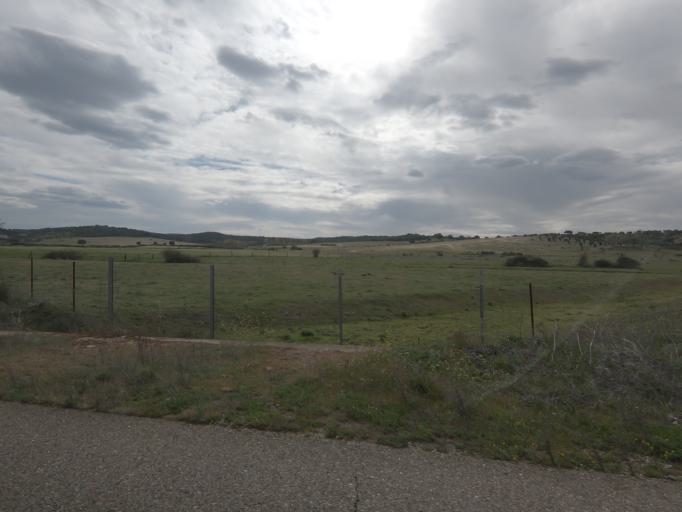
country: ES
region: Castille and Leon
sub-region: Provincia de Salamanca
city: Pastores
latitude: 40.5193
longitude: -6.5677
